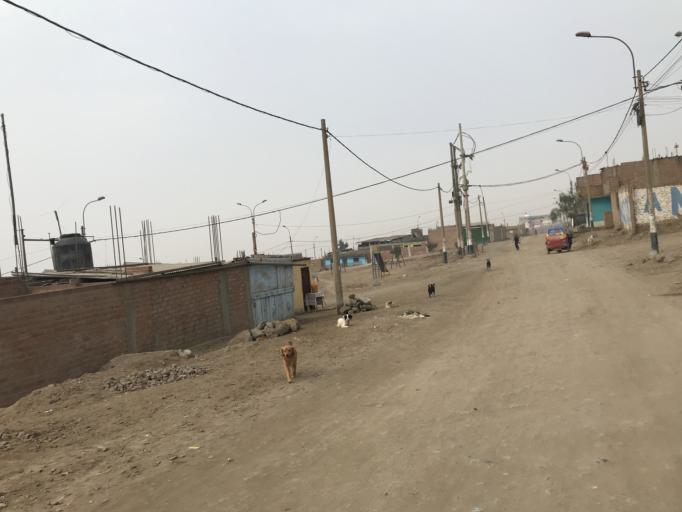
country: PE
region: Lima
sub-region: Lima
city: Carabayllo
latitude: -11.8197
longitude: -77.0435
